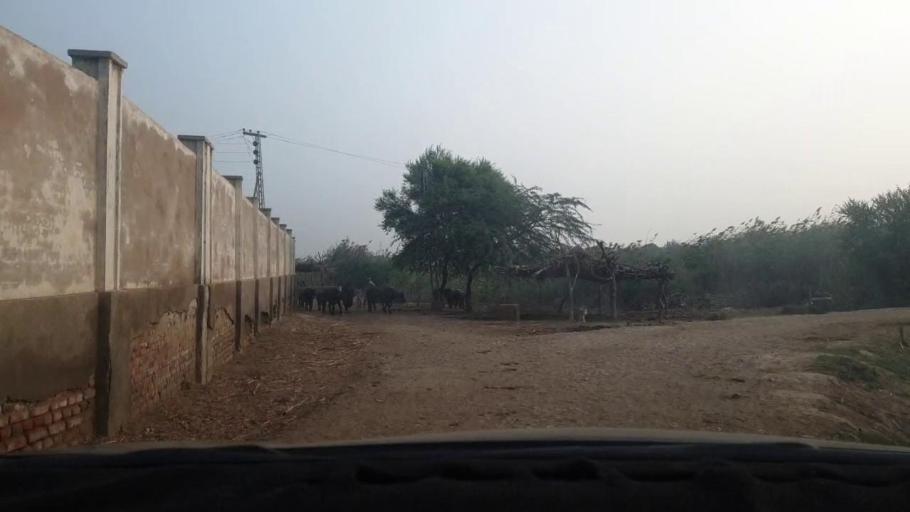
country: PK
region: Sindh
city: Matiari
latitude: 25.5843
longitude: 68.4529
